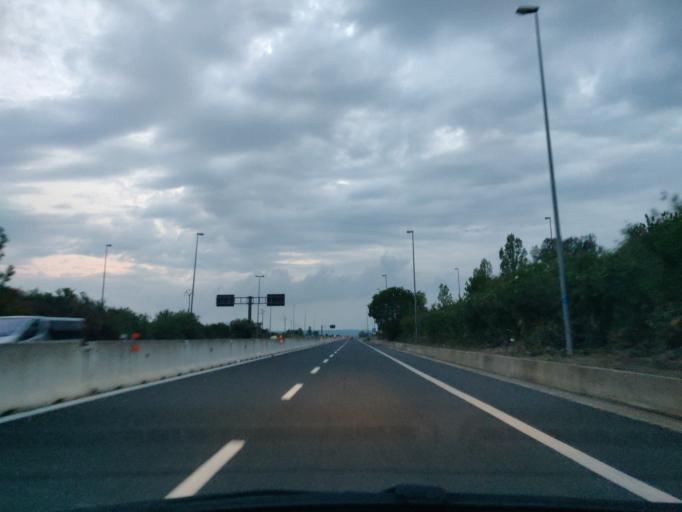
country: IT
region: Latium
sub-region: Provincia di Viterbo
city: Vetralla
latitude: 42.3632
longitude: 12.0017
